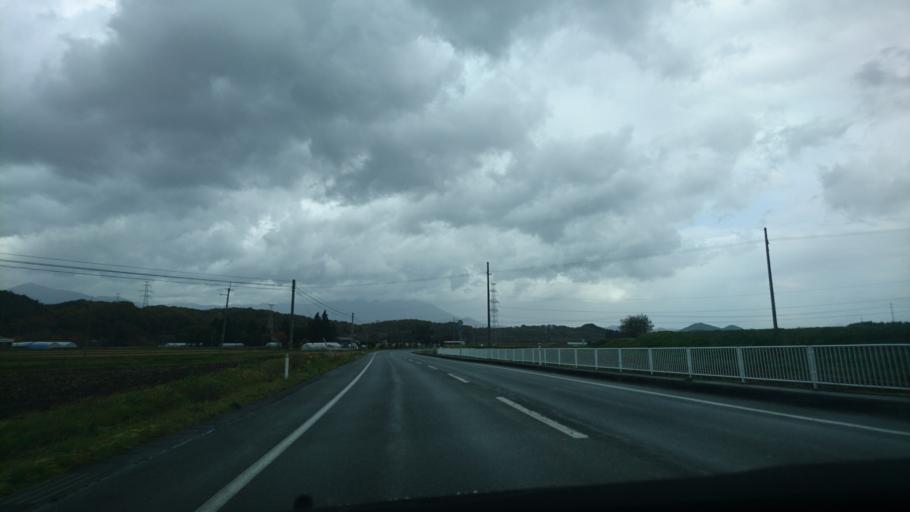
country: JP
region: Iwate
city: Shizukuishi
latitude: 39.6528
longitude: 140.9566
